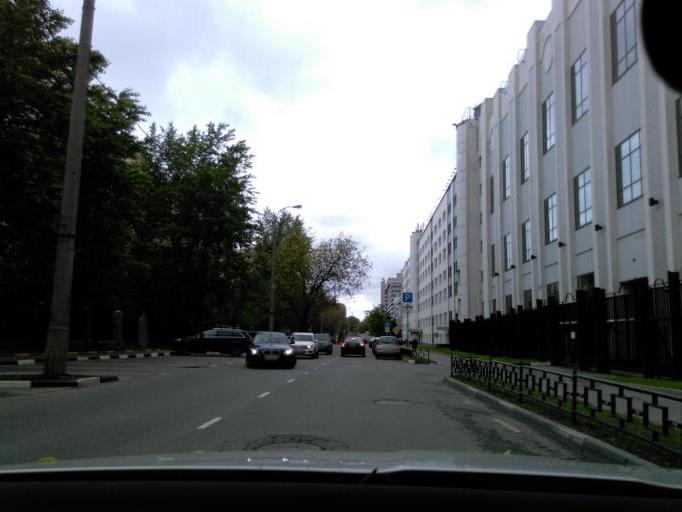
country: RU
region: Moskovskaya
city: Dorogomilovo
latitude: 55.7852
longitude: 37.5784
